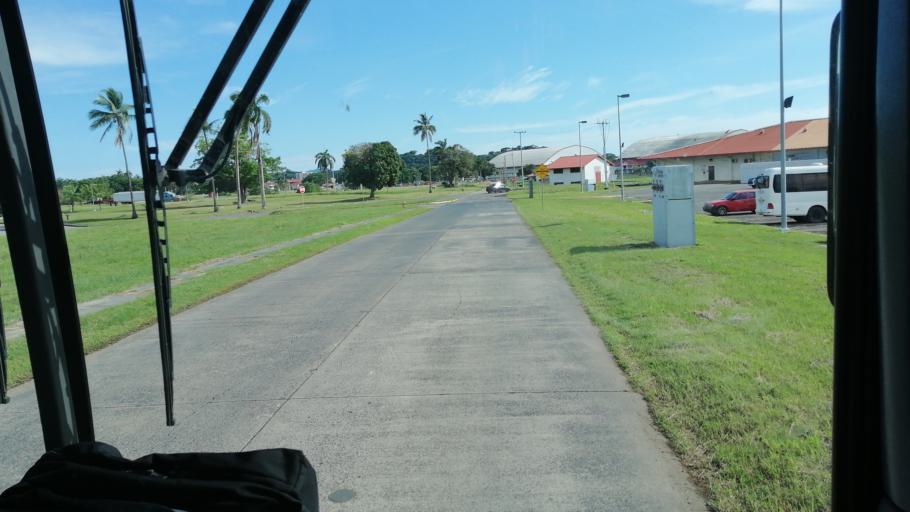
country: PA
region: Panama
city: Veracruz
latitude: 8.9184
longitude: -79.5944
